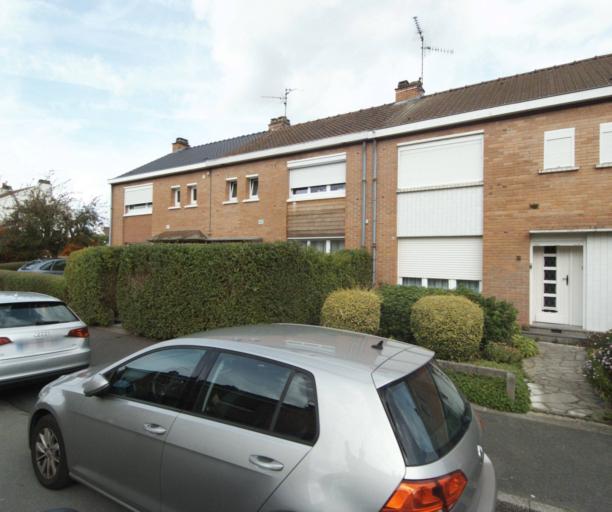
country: FR
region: Nord-Pas-de-Calais
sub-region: Departement du Nord
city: Lambersart
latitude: 50.6645
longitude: 3.0340
